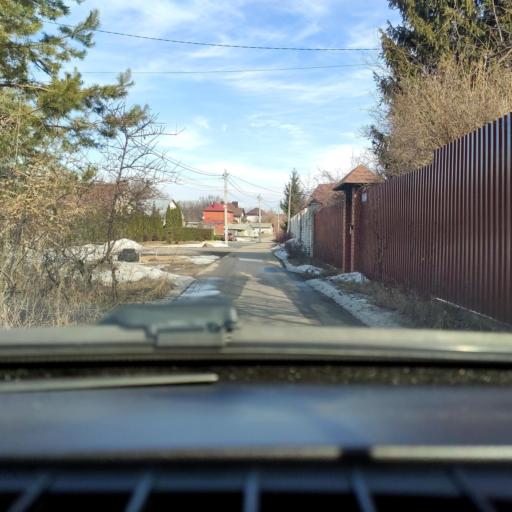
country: RU
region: Voronezj
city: Podgornoye
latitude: 51.7821
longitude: 39.1356
